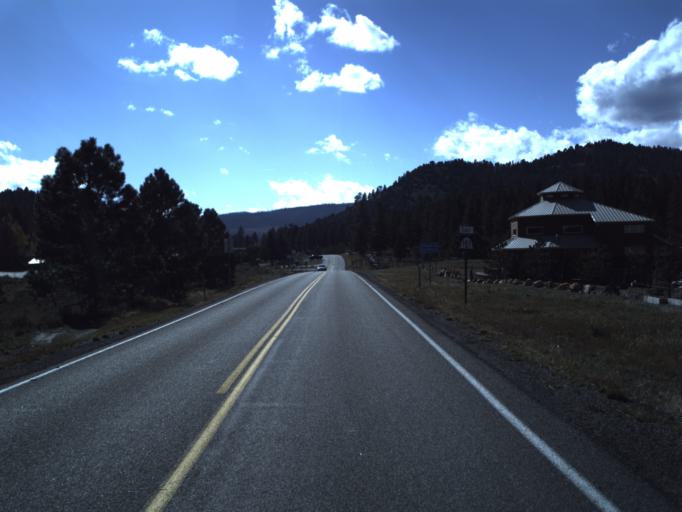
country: US
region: Utah
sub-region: Iron County
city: Parowan
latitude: 37.7037
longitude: -112.6474
